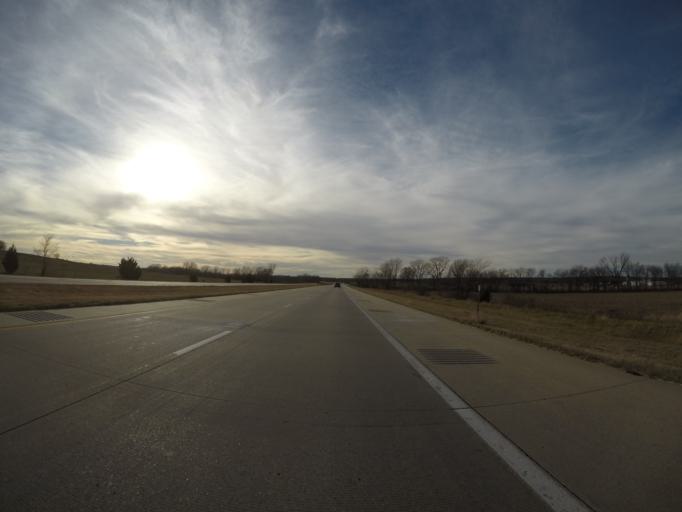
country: US
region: Kansas
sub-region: Franklin County
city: Ottawa
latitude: 38.5574
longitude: -95.3342
